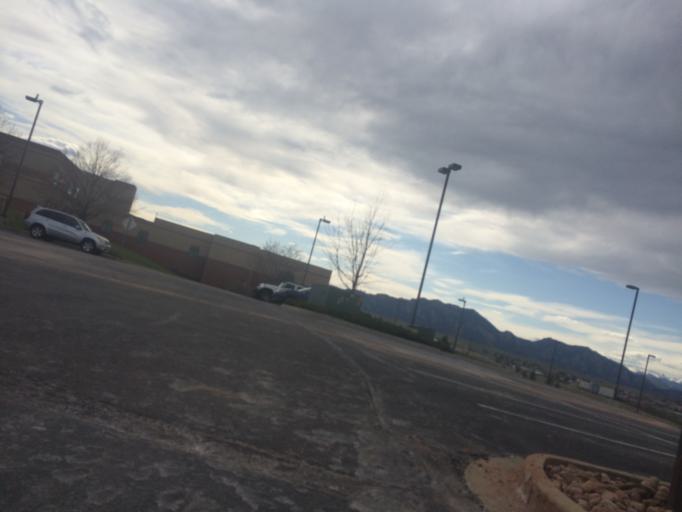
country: US
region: Colorado
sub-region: Boulder County
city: Superior
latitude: 39.9528
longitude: -105.1508
